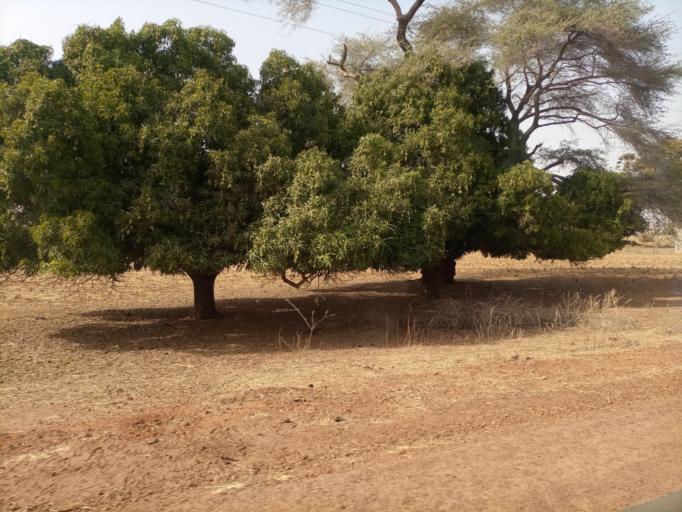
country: SN
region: Fatick
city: Foundiougne
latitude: 14.1198
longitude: -16.4441
